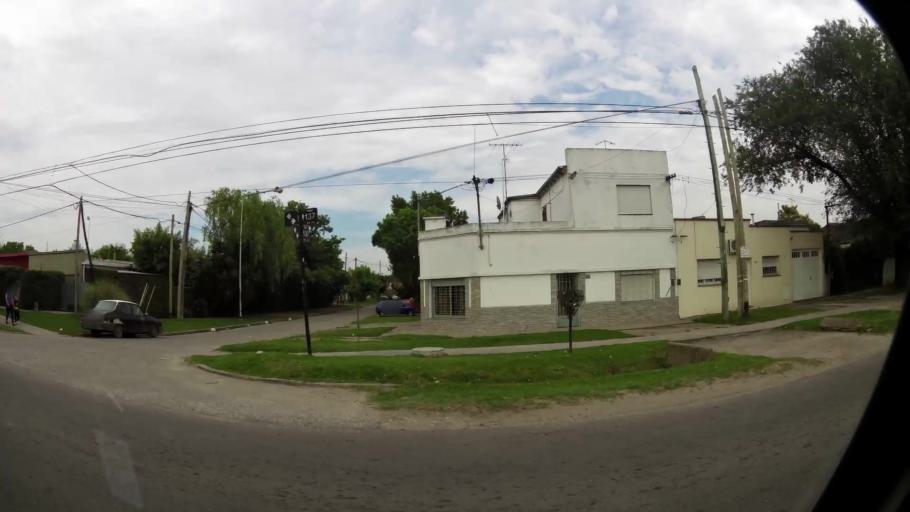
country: AR
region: Buenos Aires
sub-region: Partido de La Plata
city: La Plata
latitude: -34.9272
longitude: -58.0026
